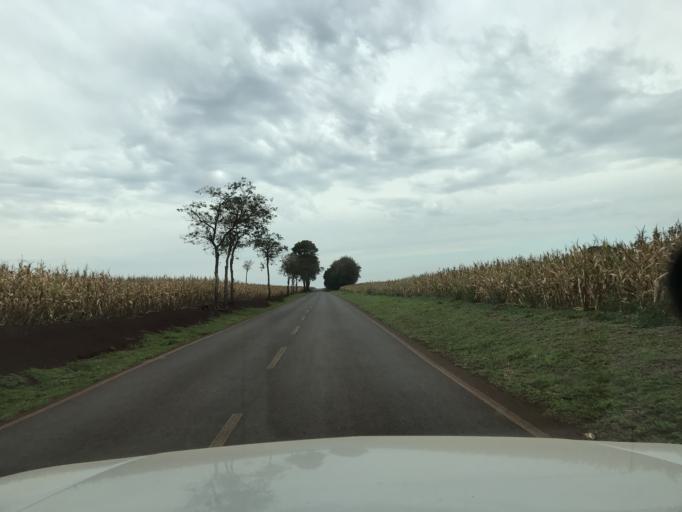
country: BR
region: Parana
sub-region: Palotina
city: Palotina
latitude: -24.4351
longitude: -53.9129
